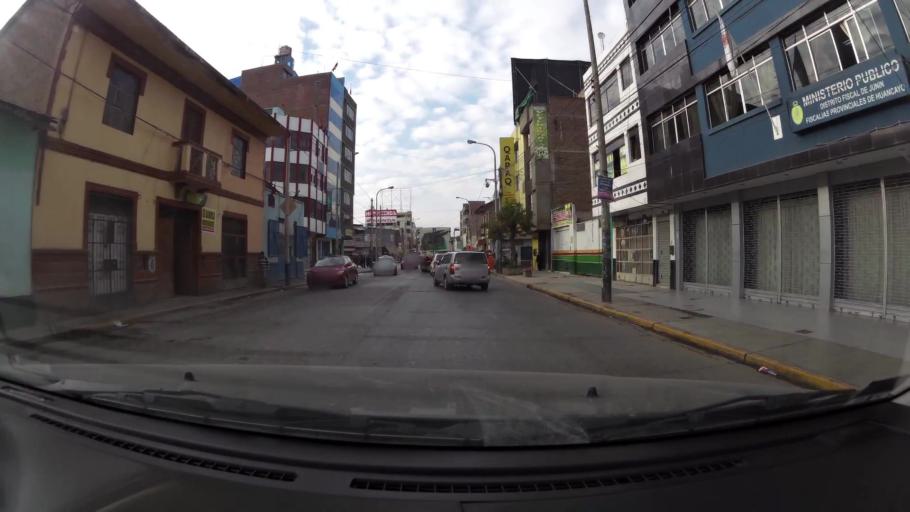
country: PE
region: Junin
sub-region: Provincia de Huancayo
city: Huancayo
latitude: -12.0758
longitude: -75.2059
